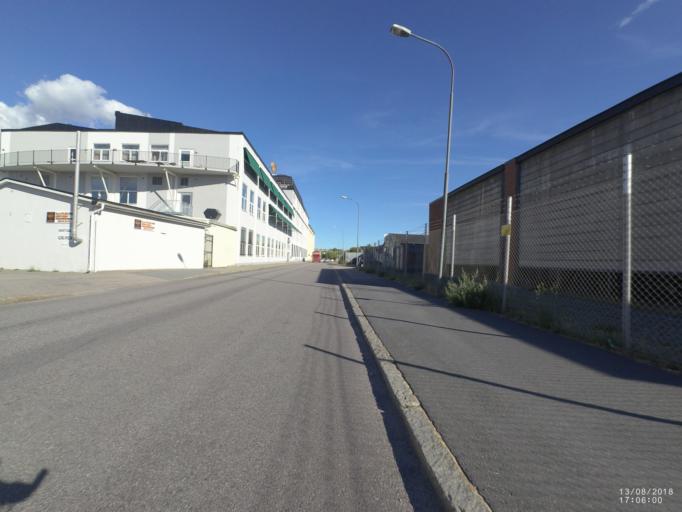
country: SE
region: Soedermanland
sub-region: Nykopings Kommun
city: Nykoping
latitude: 58.7537
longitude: 16.9920
